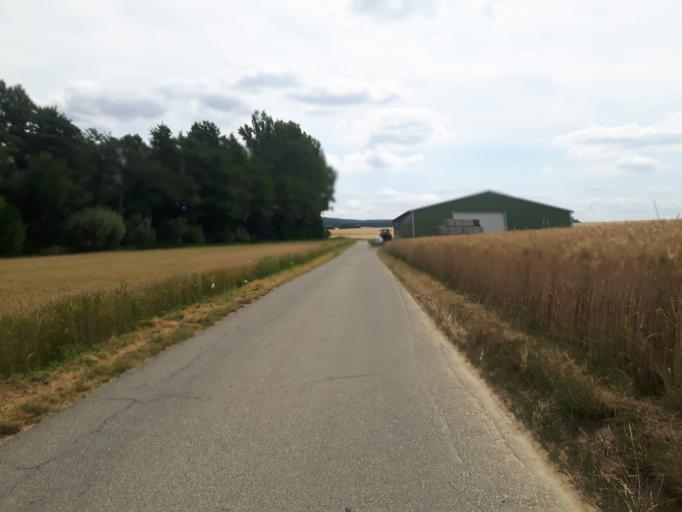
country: DE
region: Baden-Wuerttemberg
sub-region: Regierungsbezirk Stuttgart
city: Eppingen
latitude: 49.1240
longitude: 8.8896
